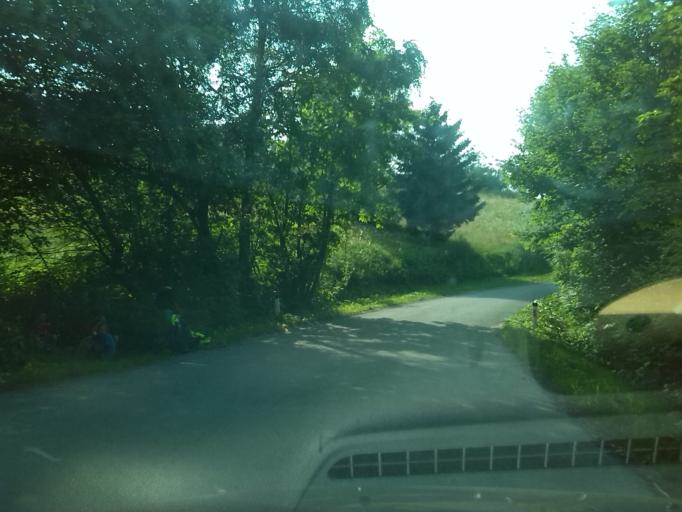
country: IT
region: Friuli Venezia Giulia
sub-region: Provincia di Udine
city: Cras
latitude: 46.1885
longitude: 13.6492
